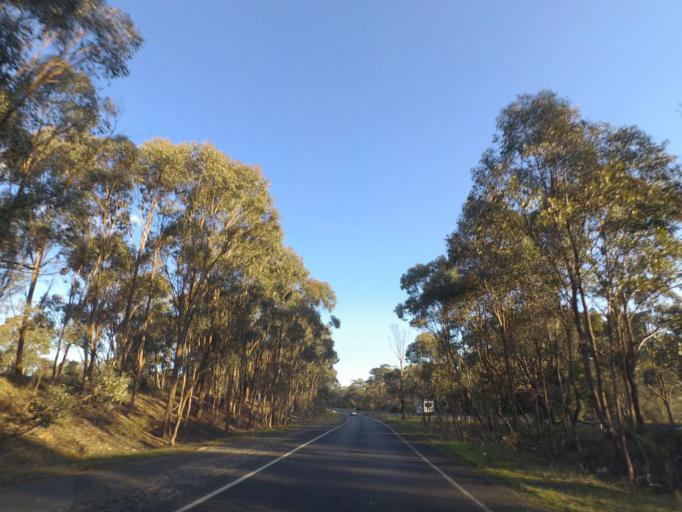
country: AU
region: Victoria
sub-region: Murrindindi
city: Kinglake West
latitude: -37.0664
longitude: 145.1019
